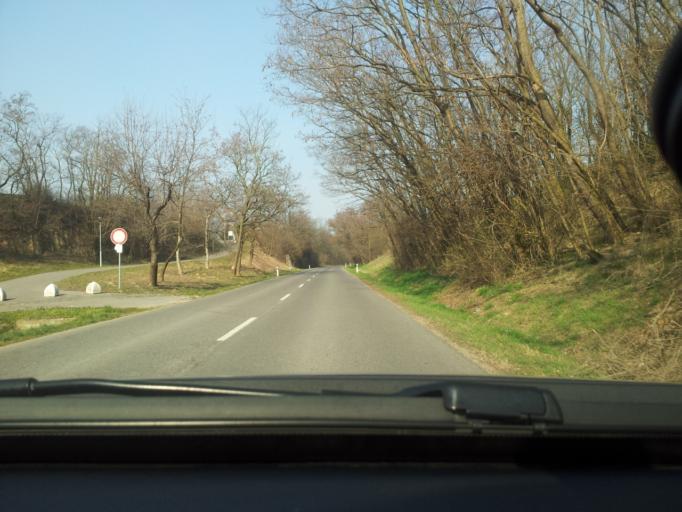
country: SK
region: Trnavsky
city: Leopoldov
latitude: 48.4601
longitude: 17.7118
